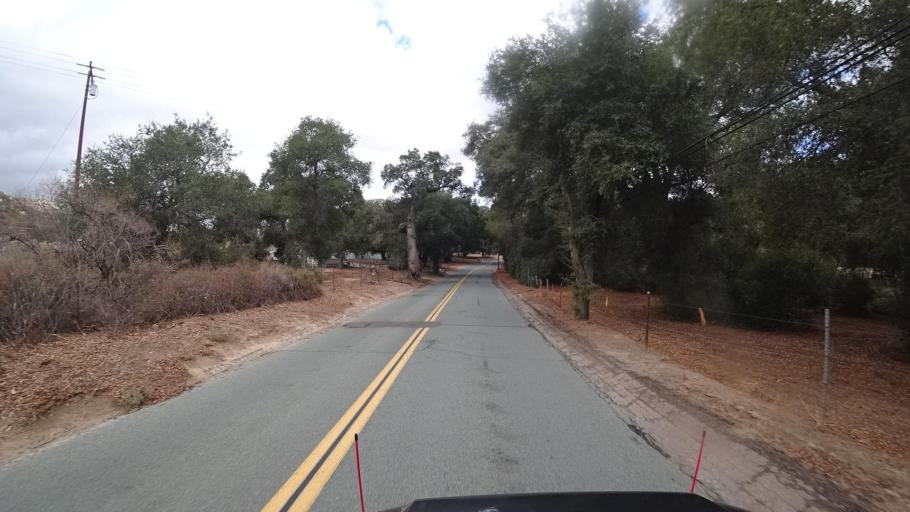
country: US
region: California
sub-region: San Diego County
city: Campo
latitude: 32.6827
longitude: -116.4312
